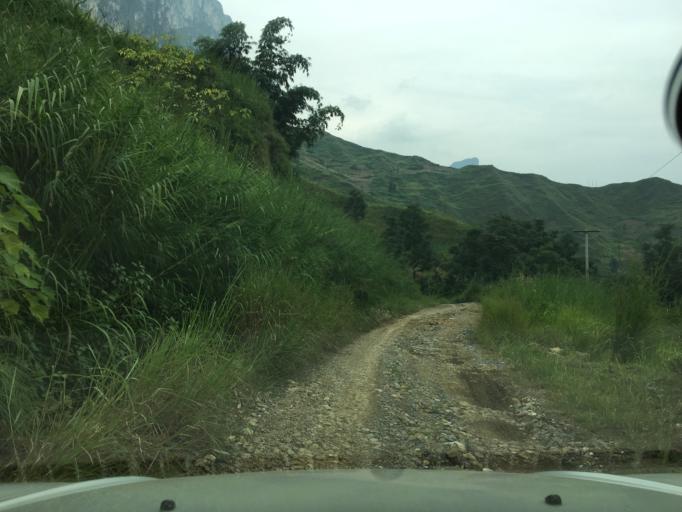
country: CN
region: Guizhou Sheng
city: Liupanshui
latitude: 26.0352
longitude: 105.1859
